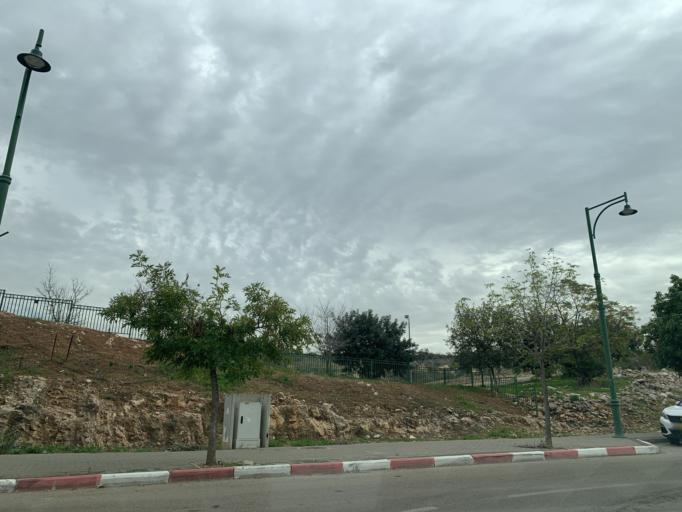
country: IL
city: Nirit
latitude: 32.1489
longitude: 34.9872
